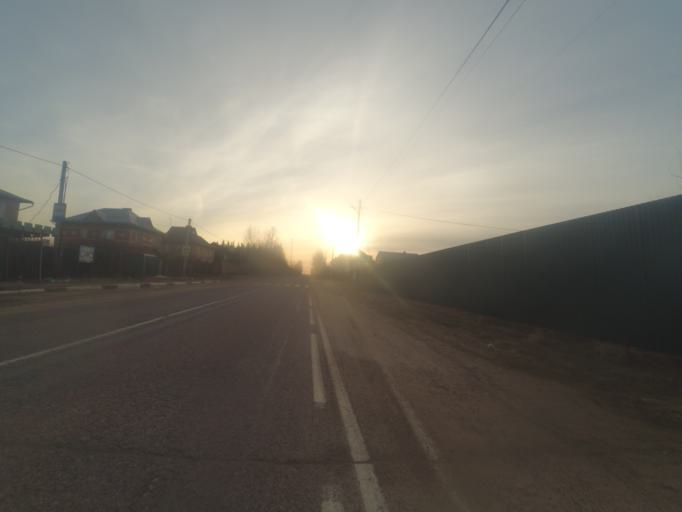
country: RU
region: Moskovskaya
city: Karinskoye
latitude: 55.7852
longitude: 36.6694
